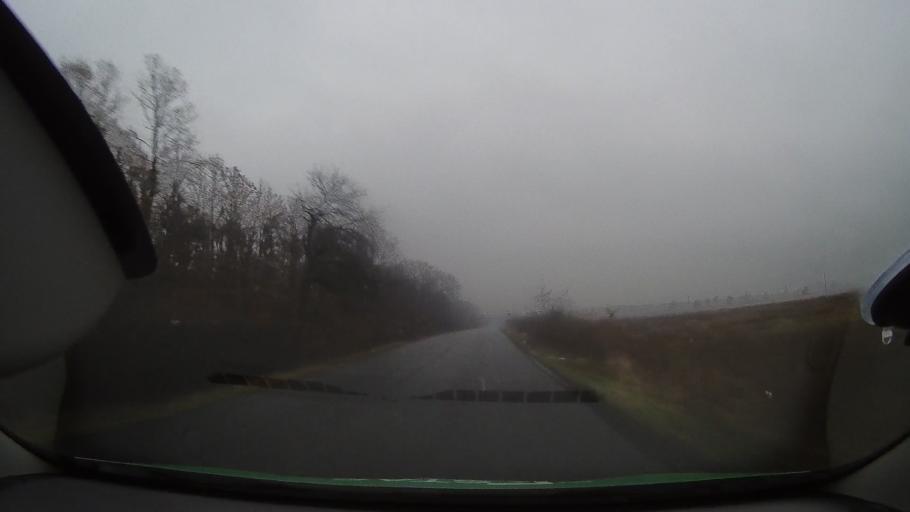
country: RO
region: Bihor
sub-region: Comuna Tinca
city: Gurbediu
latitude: 46.7783
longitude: 21.8765
